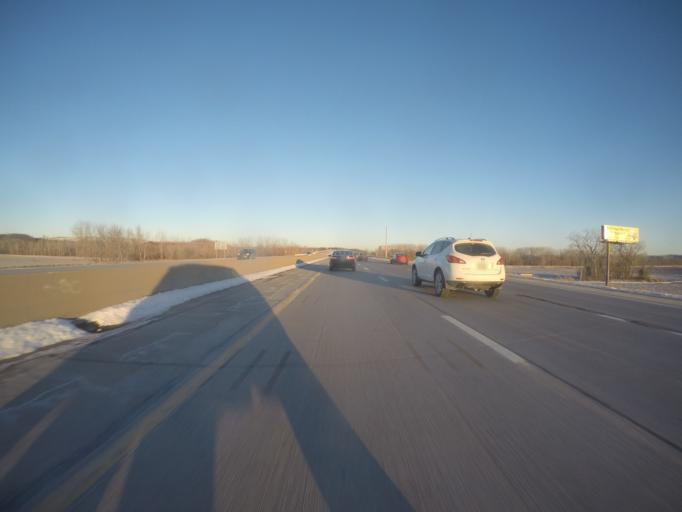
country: US
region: Missouri
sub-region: Platte County
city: Weatherby Lake
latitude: 39.1903
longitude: -94.7773
